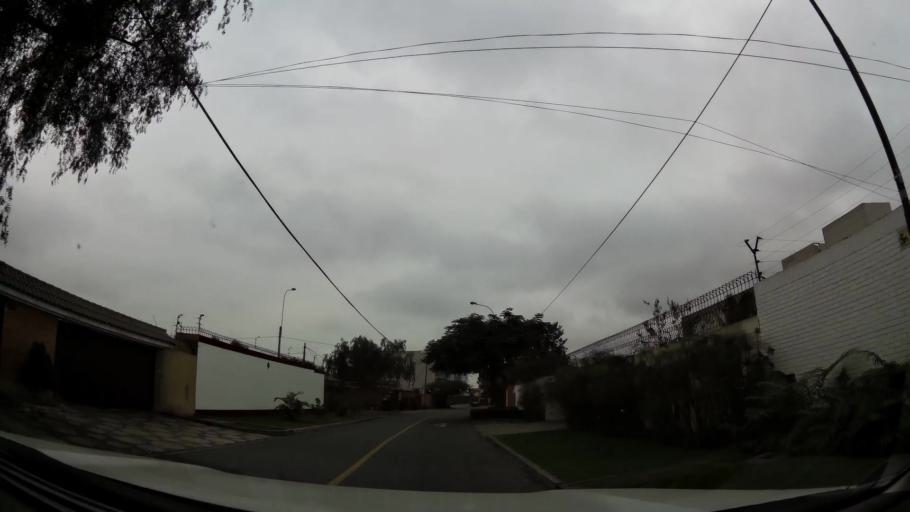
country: PE
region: Lima
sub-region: Lima
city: La Molina
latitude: -12.0695
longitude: -76.9632
